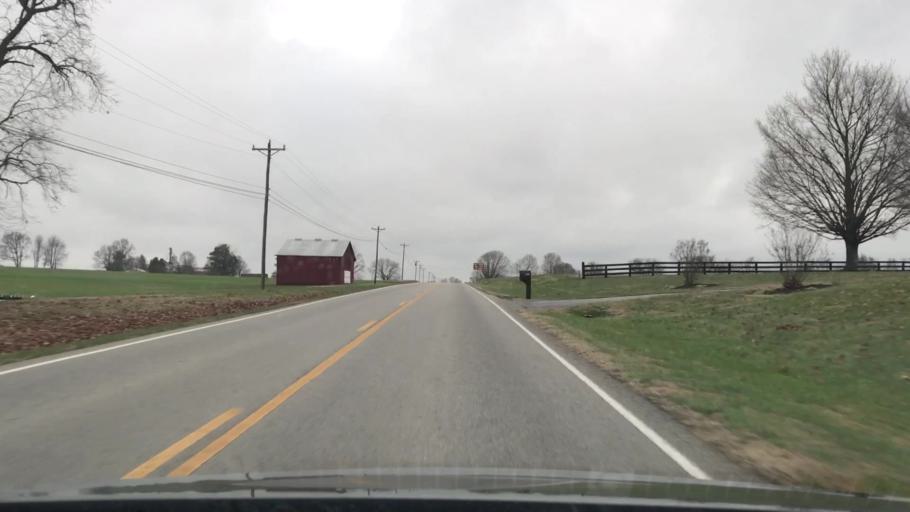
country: US
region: Kentucky
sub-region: Todd County
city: Elkton
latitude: 36.7625
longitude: -87.1672
